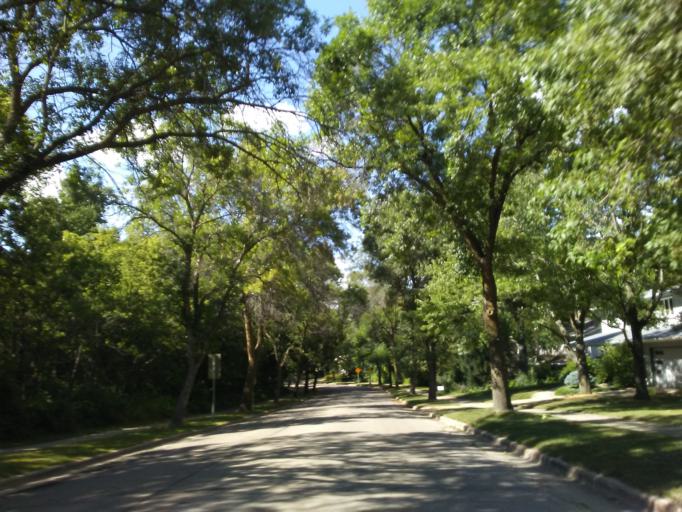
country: US
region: Wisconsin
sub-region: Dane County
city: Middleton
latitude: 43.0685
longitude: -89.4933
